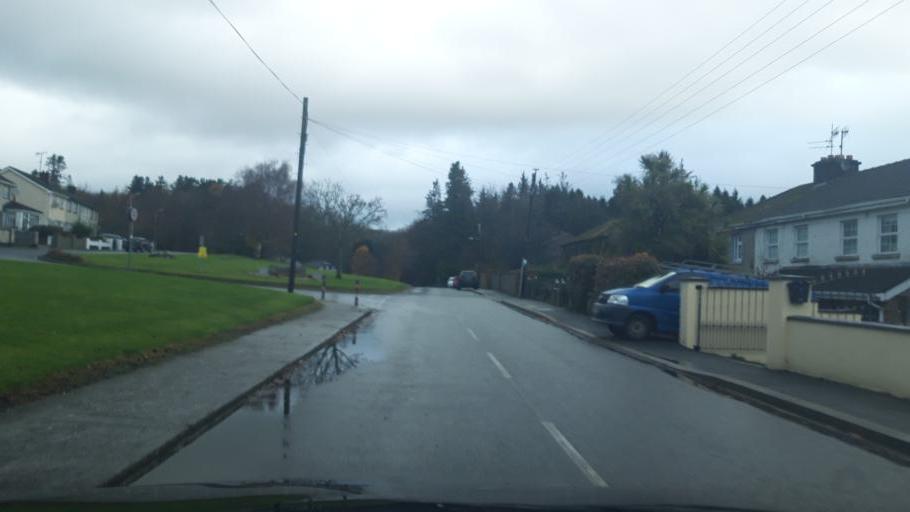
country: IE
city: Newtownmountkennedy
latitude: 53.0951
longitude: -6.1128
